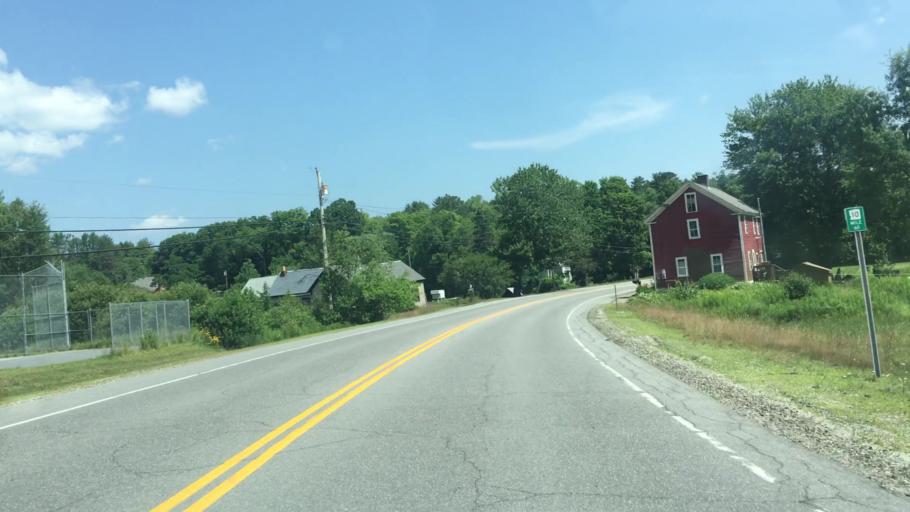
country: US
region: New Hampshire
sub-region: Sullivan County
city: Grantham
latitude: 43.4510
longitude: -72.1620
